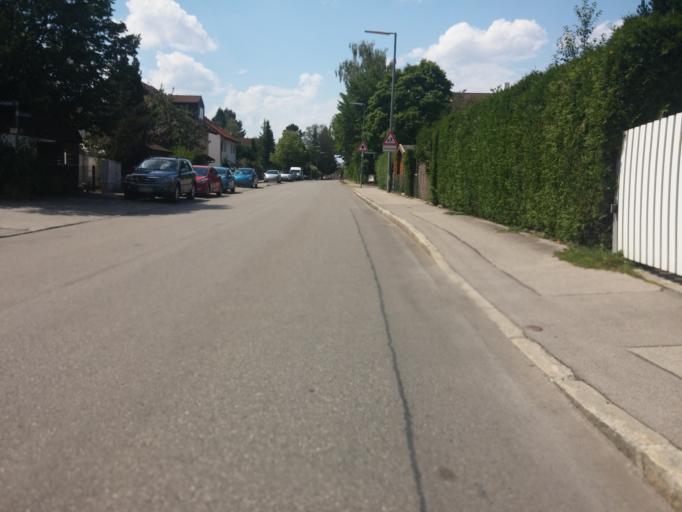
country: DE
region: Bavaria
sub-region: Upper Bavaria
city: Neubiberg
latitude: 48.1091
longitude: 11.6622
